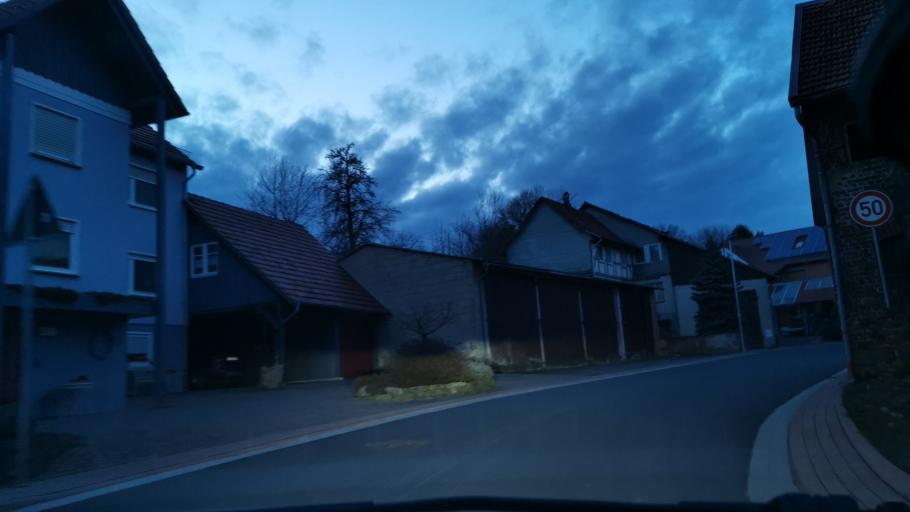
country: DE
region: Hesse
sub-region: Regierungsbezirk Kassel
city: Cornberg
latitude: 51.0688
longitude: 9.8192
